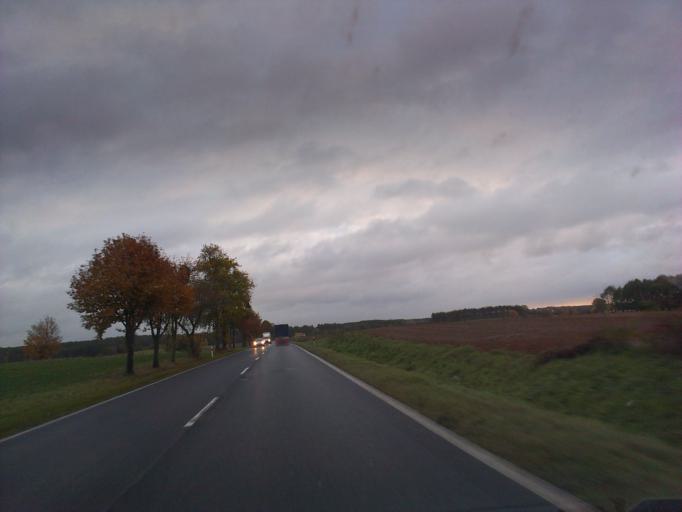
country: PL
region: Kujawsko-Pomorskie
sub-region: Powiat tucholski
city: Lubiewo
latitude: 53.5032
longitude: 18.0152
